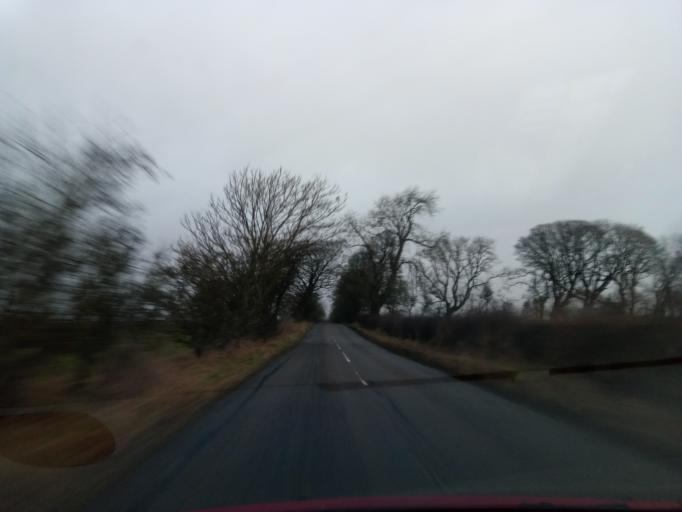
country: GB
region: England
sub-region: Northumberland
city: Rothley
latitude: 55.1939
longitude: -1.9717
